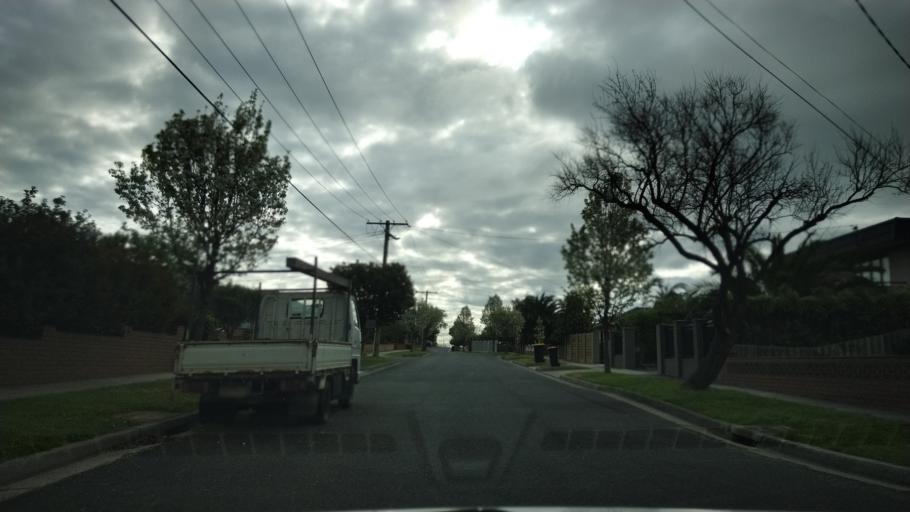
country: AU
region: Victoria
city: Highett
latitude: -37.9552
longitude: 145.0711
